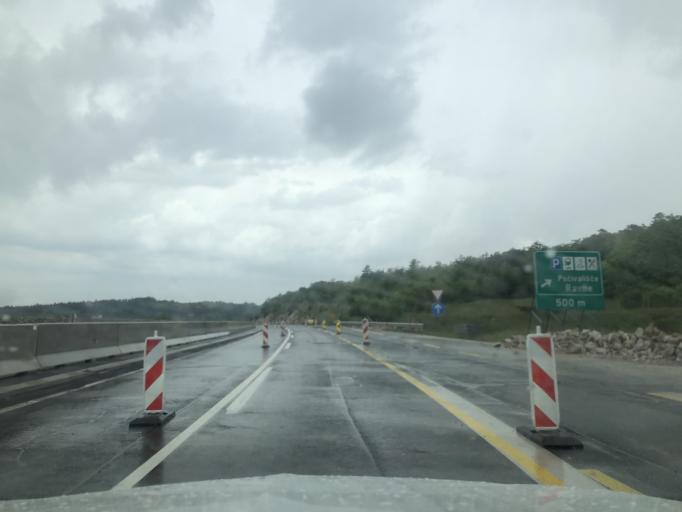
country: SI
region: Hrpelje-Kozina
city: Kozina
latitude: 45.6129
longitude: 13.9360
